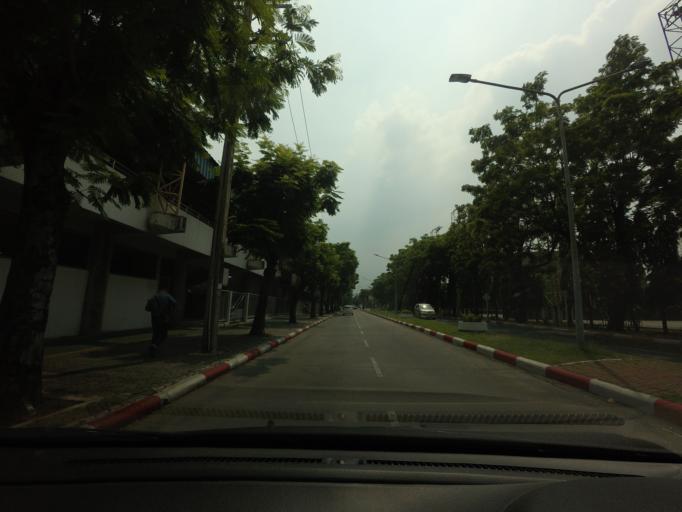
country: TH
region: Bangkok
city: Chatuchak
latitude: 13.8515
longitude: 100.5657
